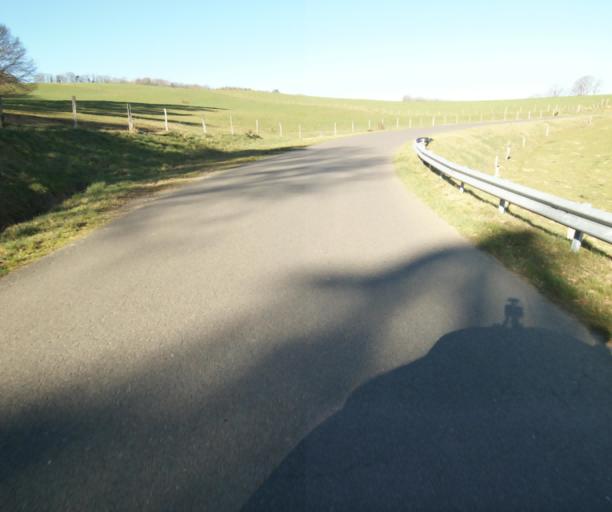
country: FR
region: Limousin
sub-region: Departement de la Correze
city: Chamboulive
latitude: 45.4113
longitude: 1.6676
